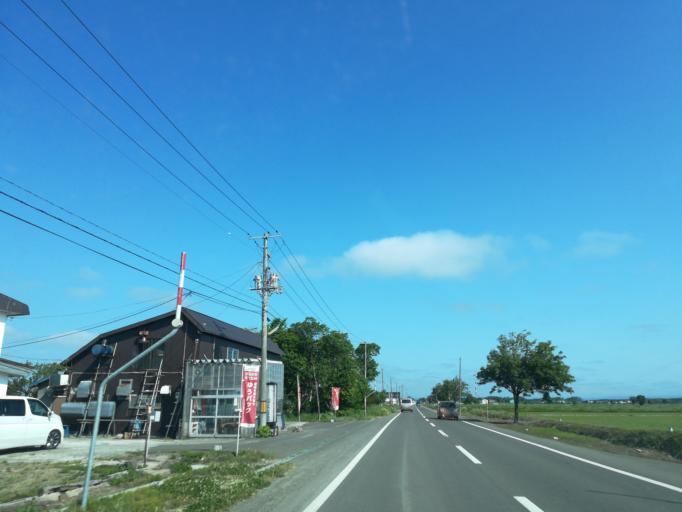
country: JP
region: Hokkaido
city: Iwamizawa
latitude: 43.1680
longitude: 141.7335
